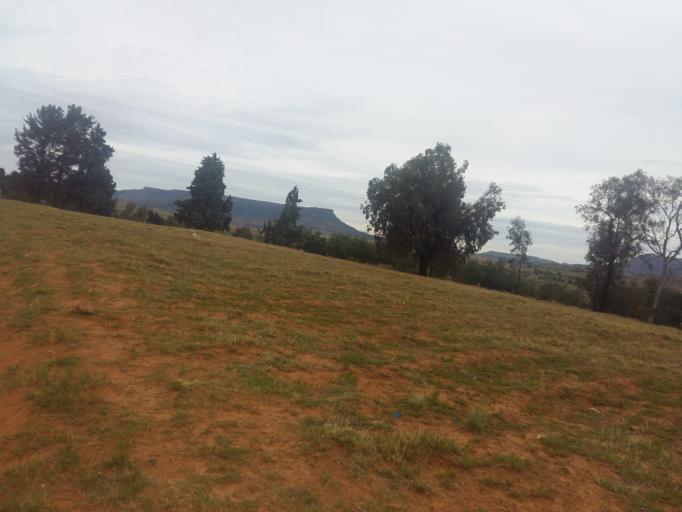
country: LS
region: Mafeteng
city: Mafeteng
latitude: -29.6953
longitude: 27.4329
